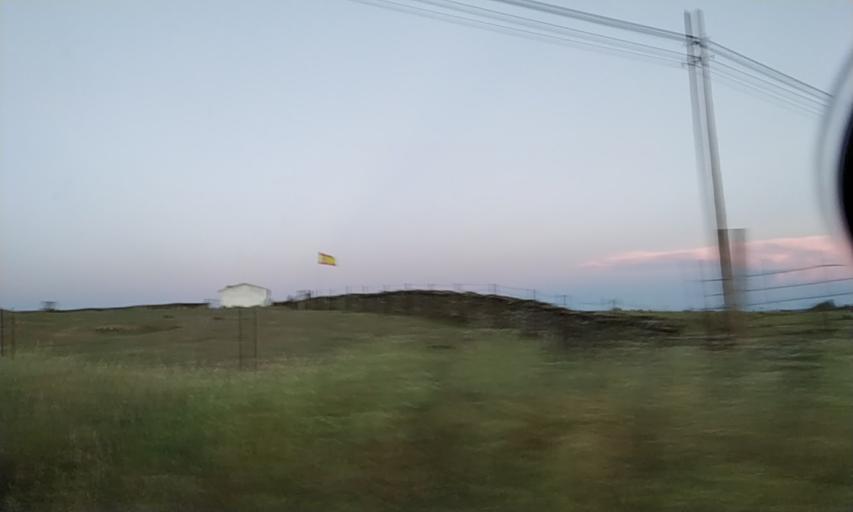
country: ES
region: Extremadura
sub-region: Provincia de Caceres
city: Alcantara
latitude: 39.7366
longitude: -6.9058
